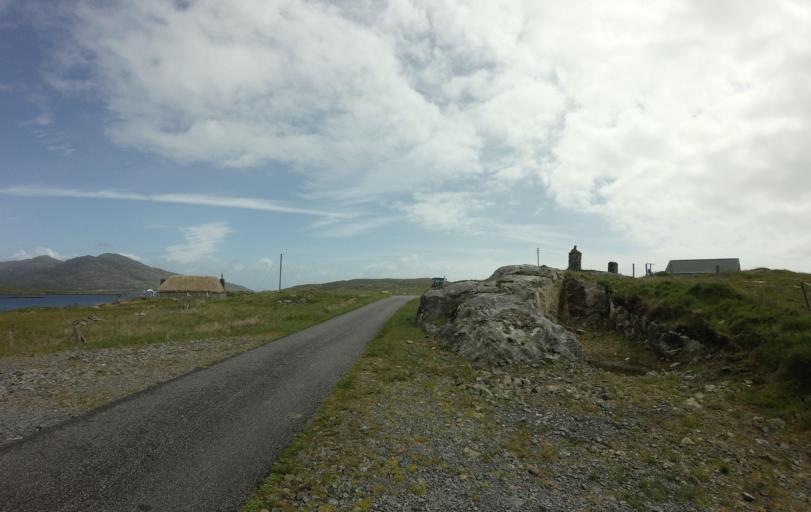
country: GB
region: Scotland
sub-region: Eilean Siar
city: Isle of South Uist
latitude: 57.1356
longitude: -7.3164
